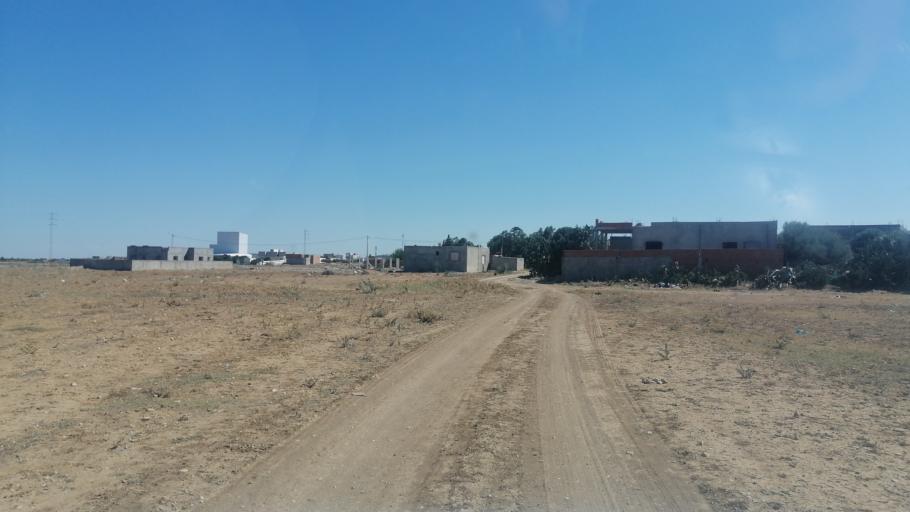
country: TN
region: Al Qayrawan
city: Sbikha
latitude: 36.1284
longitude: 10.0979
